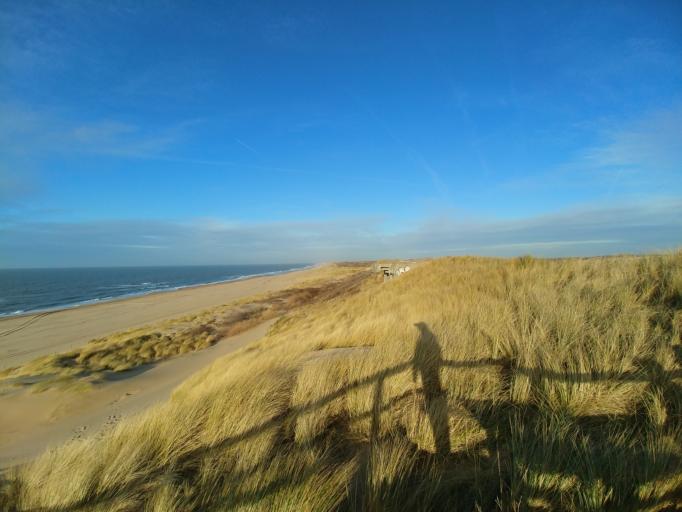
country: NL
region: South Holland
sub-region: Gemeente Den Haag
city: Scheveningen
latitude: 52.1258
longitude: 4.3012
